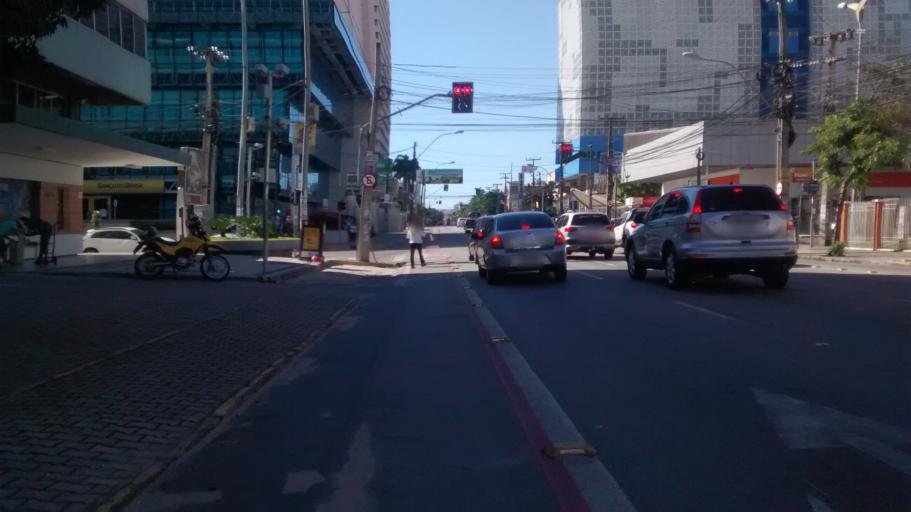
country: BR
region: Ceara
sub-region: Fortaleza
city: Fortaleza
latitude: -3.7360
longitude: -38.4988
